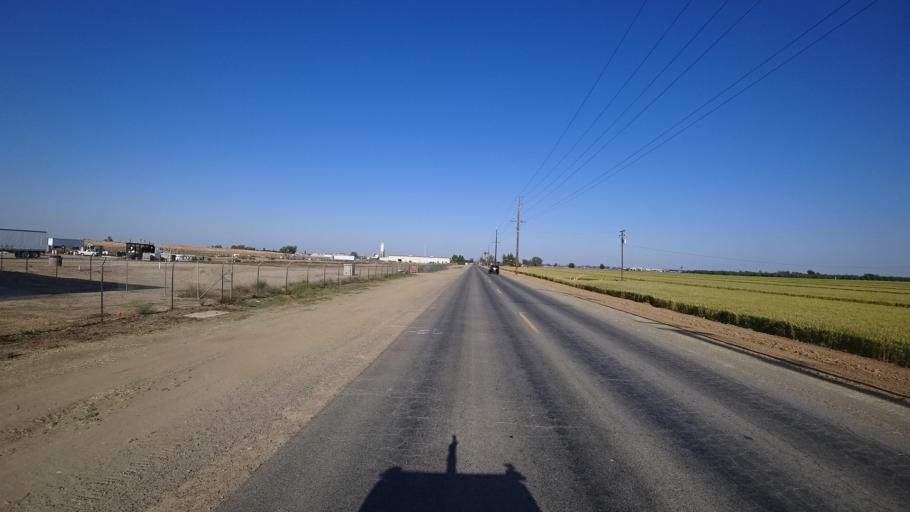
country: US
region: California
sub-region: Kings County
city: Home Garden
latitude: 36.3135
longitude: -119.5928
